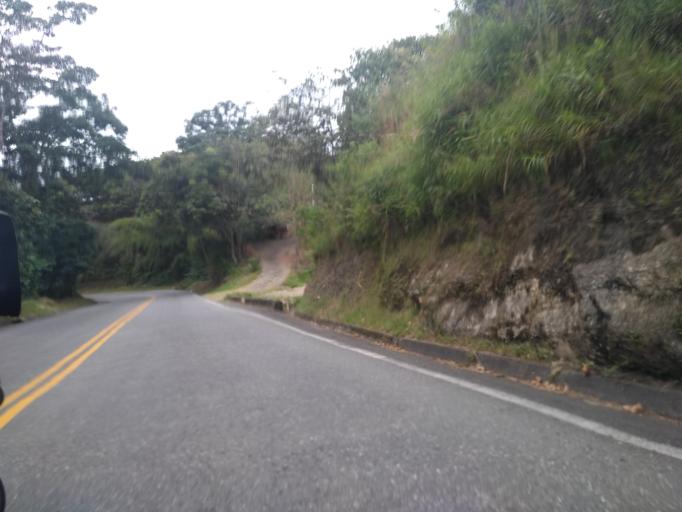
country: CO
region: Cauca
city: Rosas
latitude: 2.2429
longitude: -76.7692
